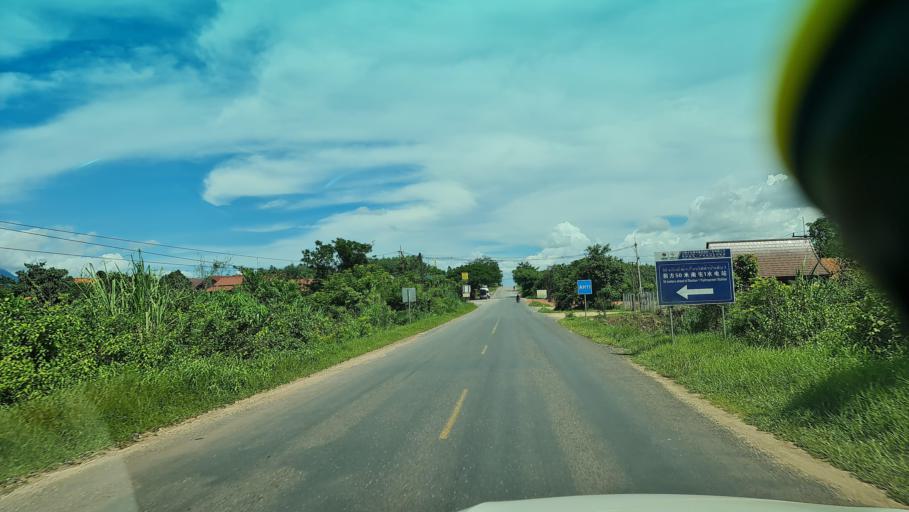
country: LA
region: Bolikhamxai
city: Ban Nahin
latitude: 18.2984
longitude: 104.1297
